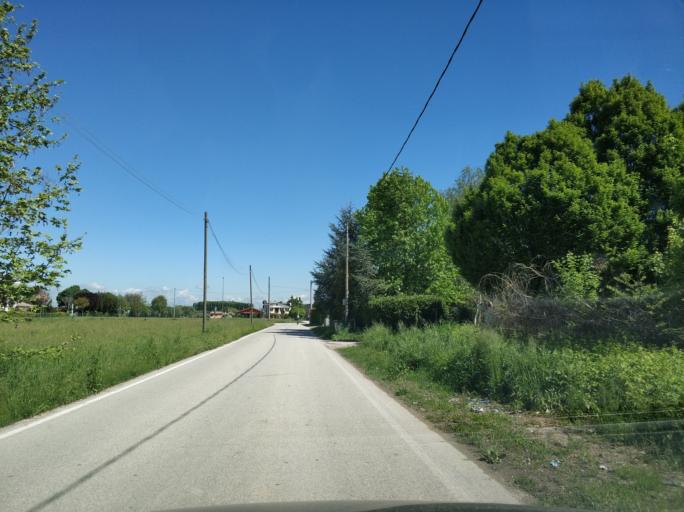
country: IT
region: Veneto
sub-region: Provincia di Venezia
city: Pianiga
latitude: 45.4404
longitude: 12.0002
